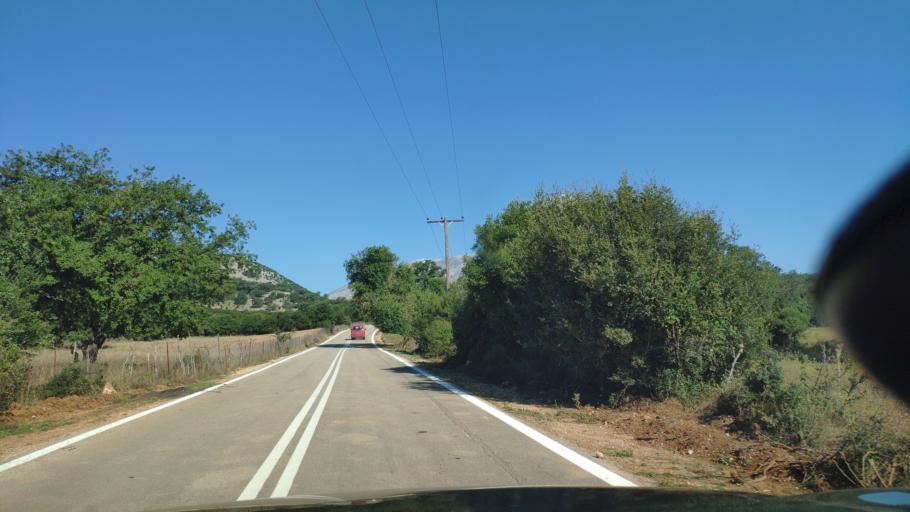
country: GR
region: West Greece
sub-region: Nomos Aitolias kai Akarnanias
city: Fitiai
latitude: 38.6852
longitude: 21.1206
